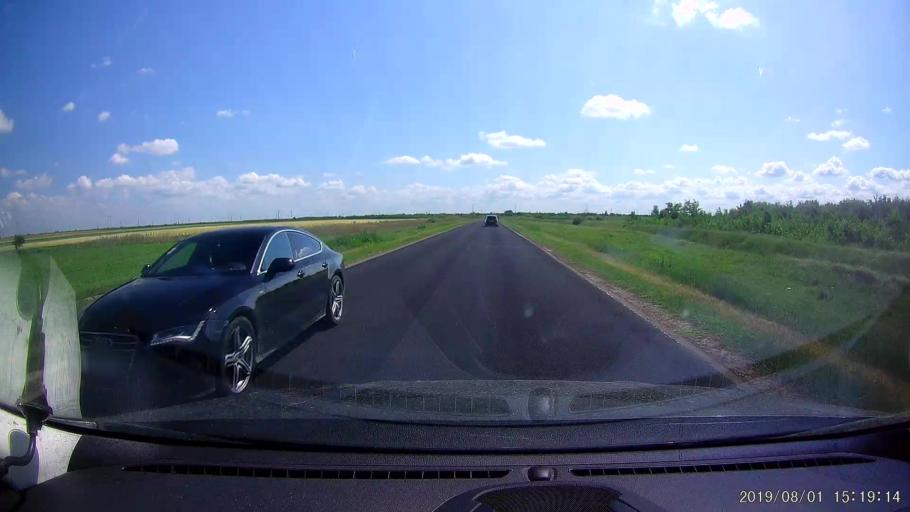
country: RO
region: Braila
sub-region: Comuna Unirea
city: Unirea
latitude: 45.0922
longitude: 27.8140
